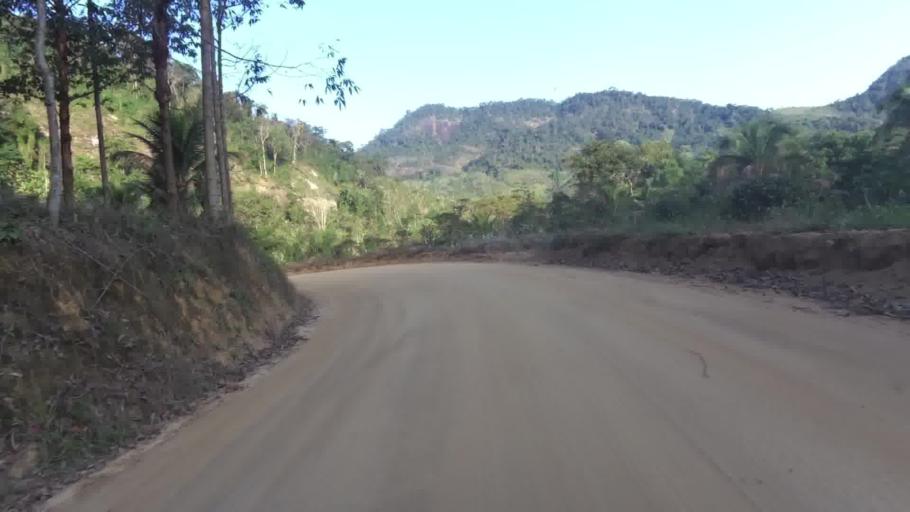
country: BR
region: Espirito Santo
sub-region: Alfredo Chaves
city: Alfredo Chaves
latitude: -20.5924
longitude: -40.6978
